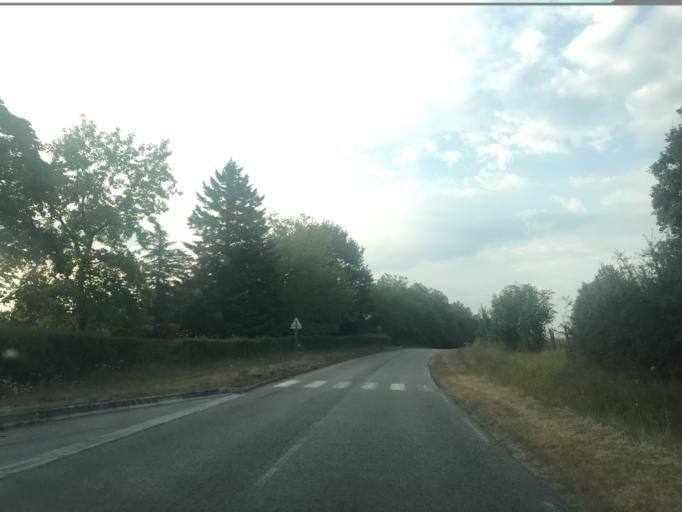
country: FR
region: Ile-de-France
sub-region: Departement des Yvelines
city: Jouars-Pontchartrain
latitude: 48.7702
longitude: 1.8782
